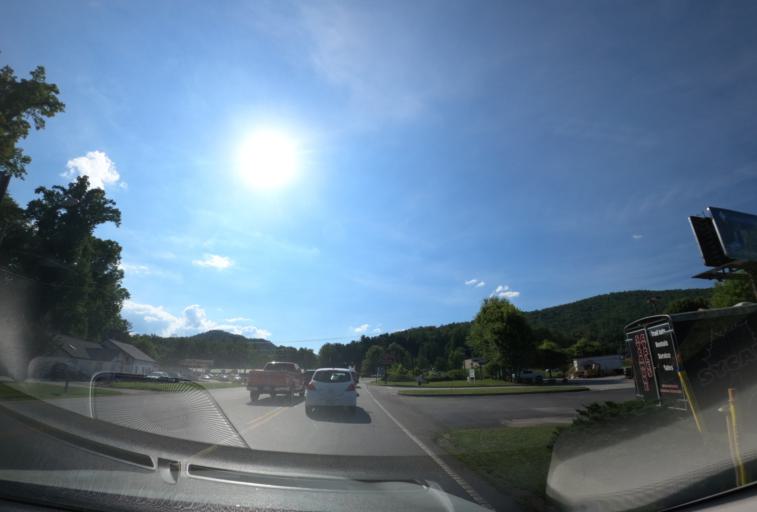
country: US
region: North Carolina
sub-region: Transylvania County
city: Brevard
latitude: 35.2735
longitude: -82.7027
